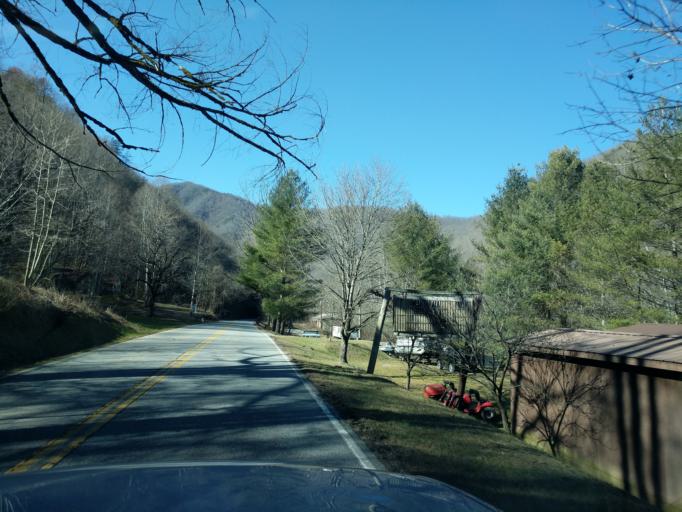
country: US
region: North Carolina
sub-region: Swain County
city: Bryson City
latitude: 35.3318
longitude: -83.6078
